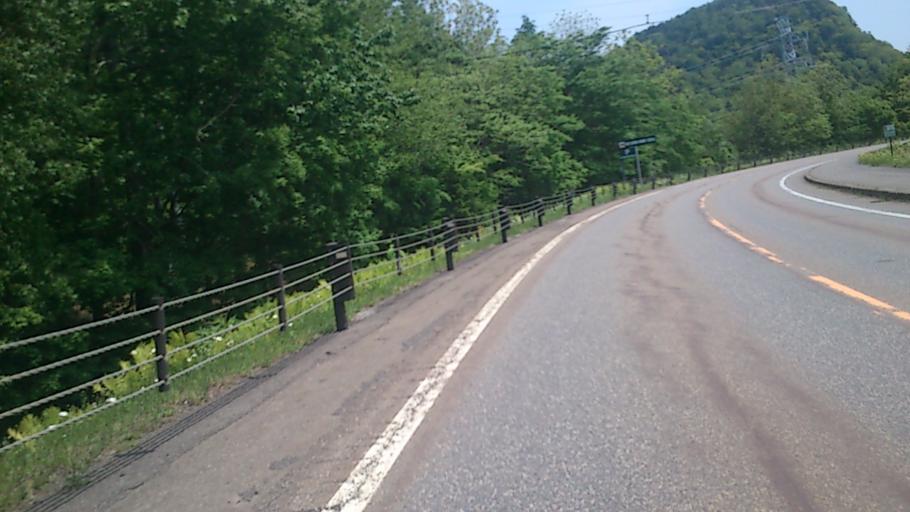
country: JP
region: Hokkaido
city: Otofuke
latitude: 43.3599
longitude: 143.2524
